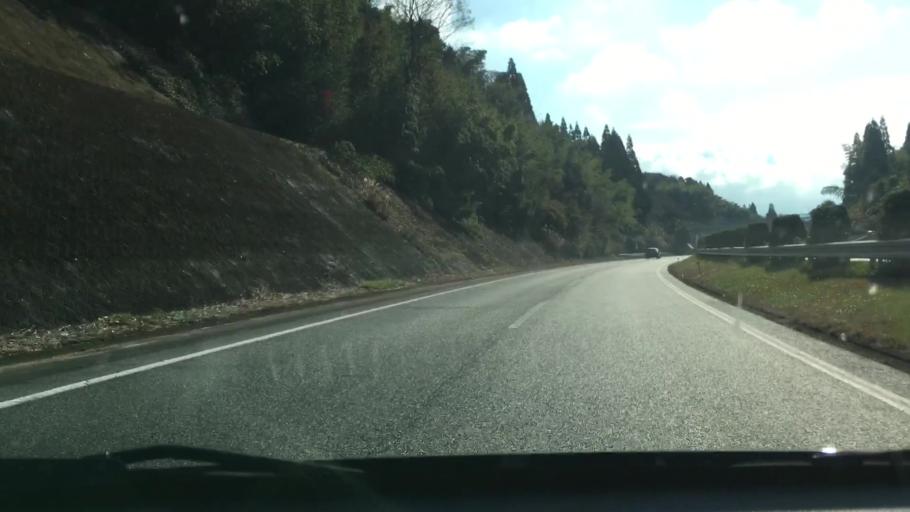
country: JP
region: Kumamoto
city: Matsubase
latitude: 32.6096
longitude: 130.7245
